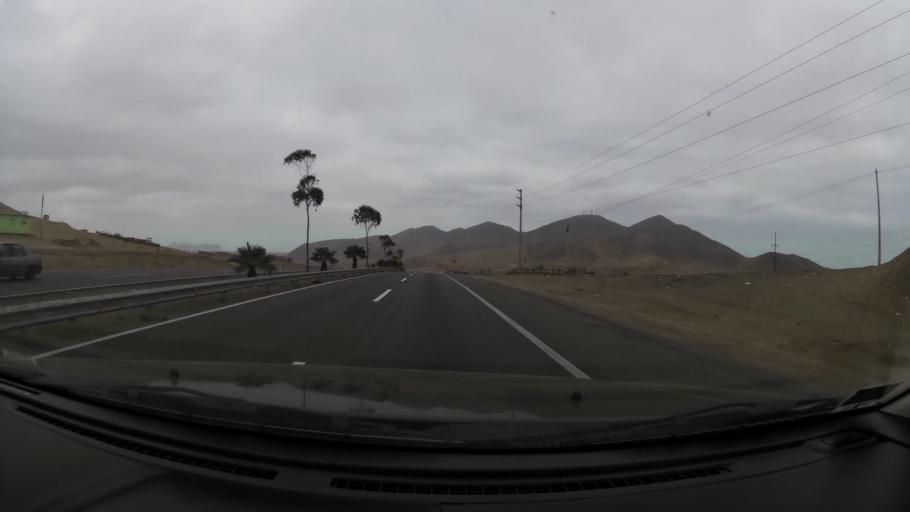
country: PE
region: Lima
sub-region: Lima
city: Pucusana
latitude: -12.4409
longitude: -76.7566
